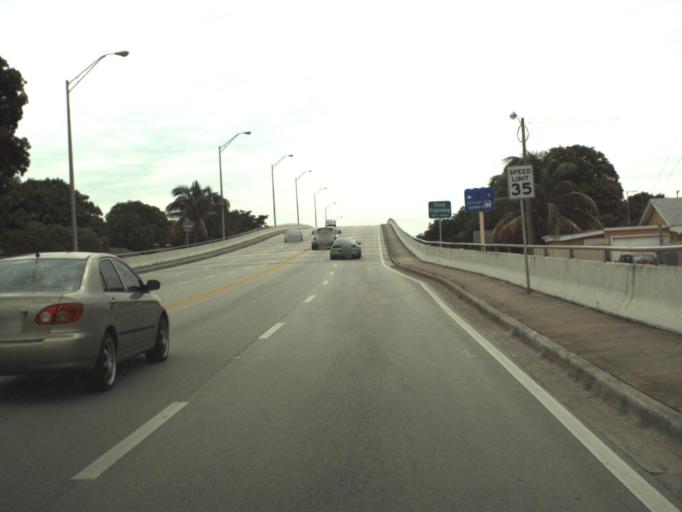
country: US
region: Florida
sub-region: Palm Beach County
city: Lake Clarke Shores
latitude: 26.6758
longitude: -80.0606
